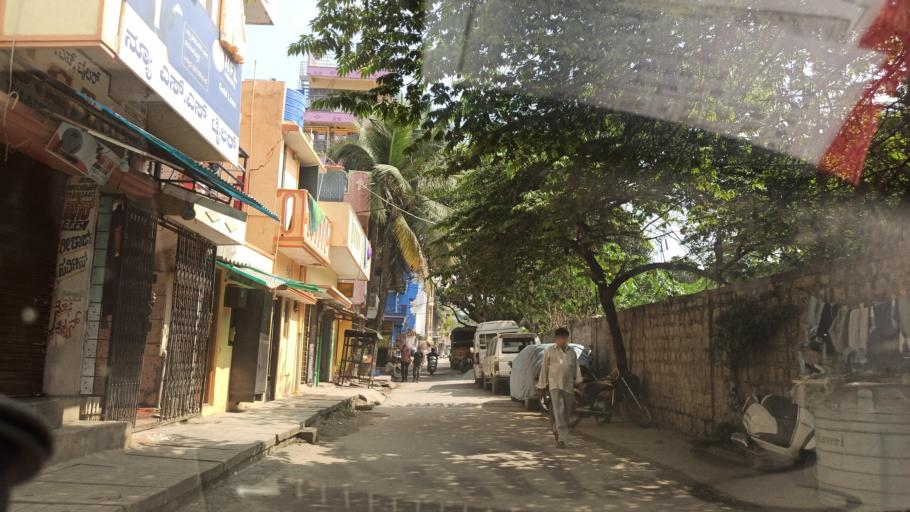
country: IN
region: Karnataka
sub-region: Bangalore Urban
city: Bangalore
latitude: 12.9575
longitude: 77.6955
